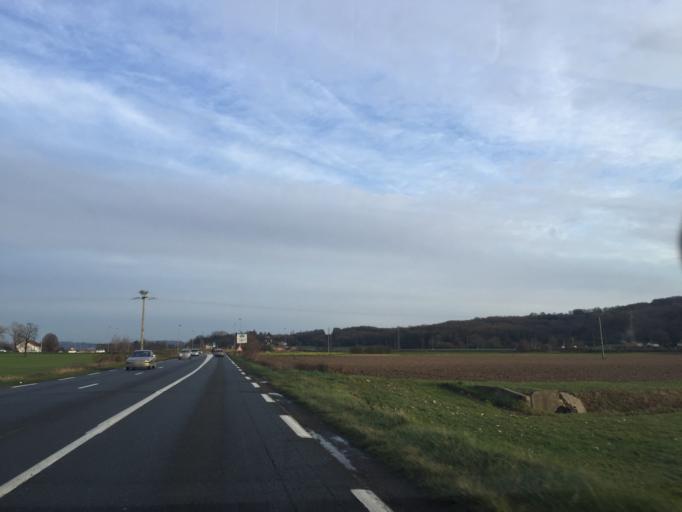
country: FR
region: Rhone-Alpes
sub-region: Departement de l'Isere
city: Vaulx-Milieu
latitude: 45.6151
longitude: 5.1937
